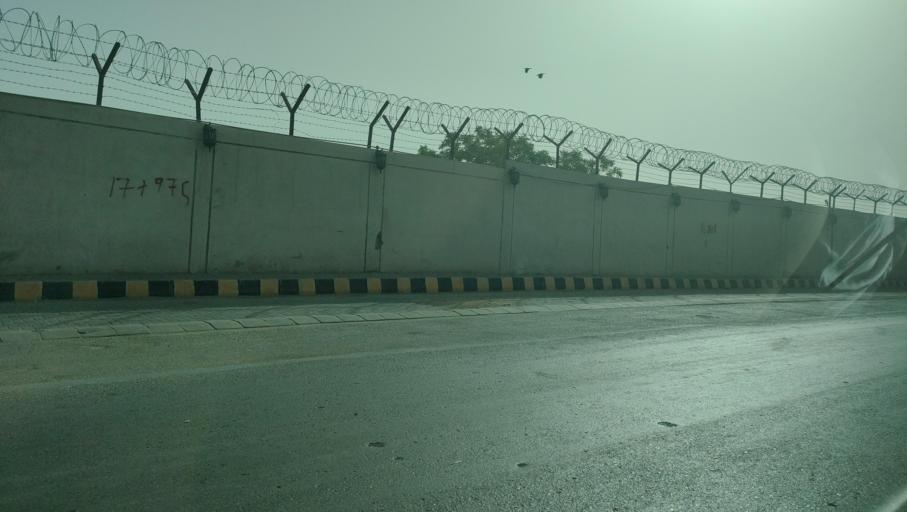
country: PK
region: Sindh
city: Malir Cantonment
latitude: 24.9221
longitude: 67.1848
